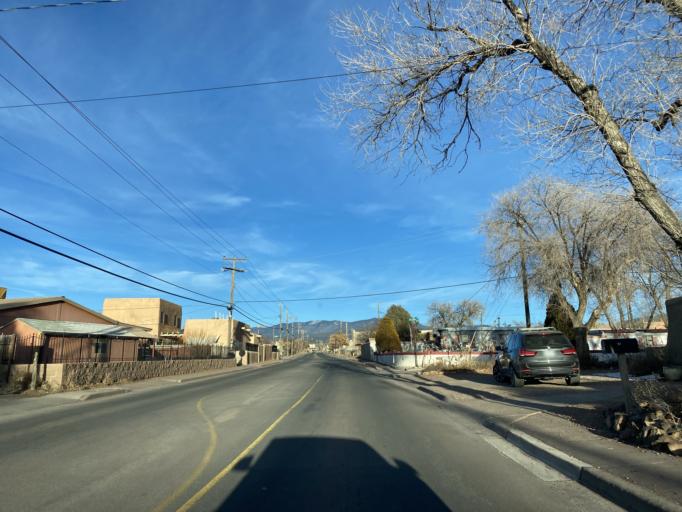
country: US
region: New Mexico
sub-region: Santa Fe County
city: Santa Fe
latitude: 35.6744
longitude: -105.9754
